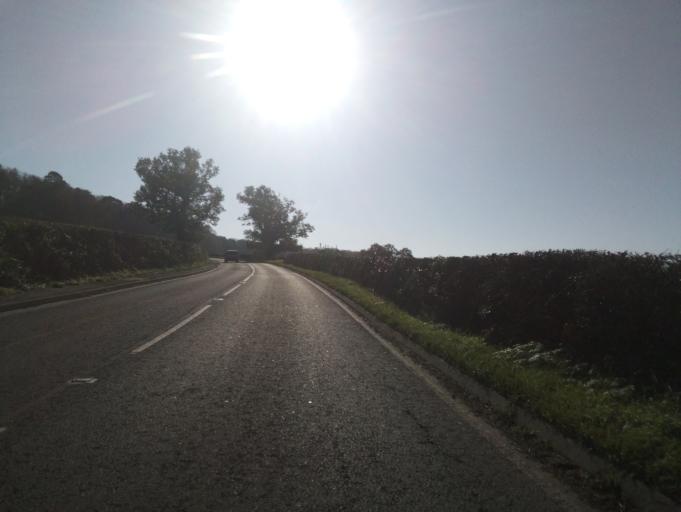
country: GB
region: England
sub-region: Dorset
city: Sherborne
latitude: 50.9356
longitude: -2.5121
